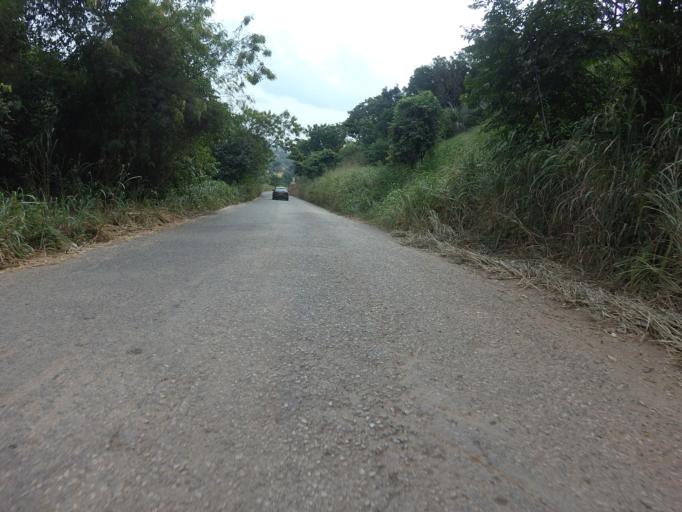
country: GH
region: Volta
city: Ho
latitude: 6.6842
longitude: 0.3418
